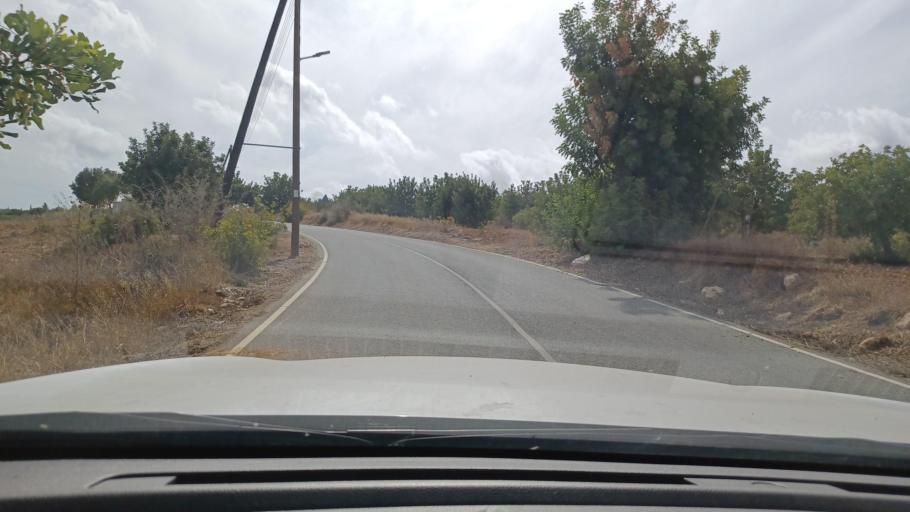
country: CY
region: Pafos
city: Polis
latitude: 34.9501
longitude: 32.4465
